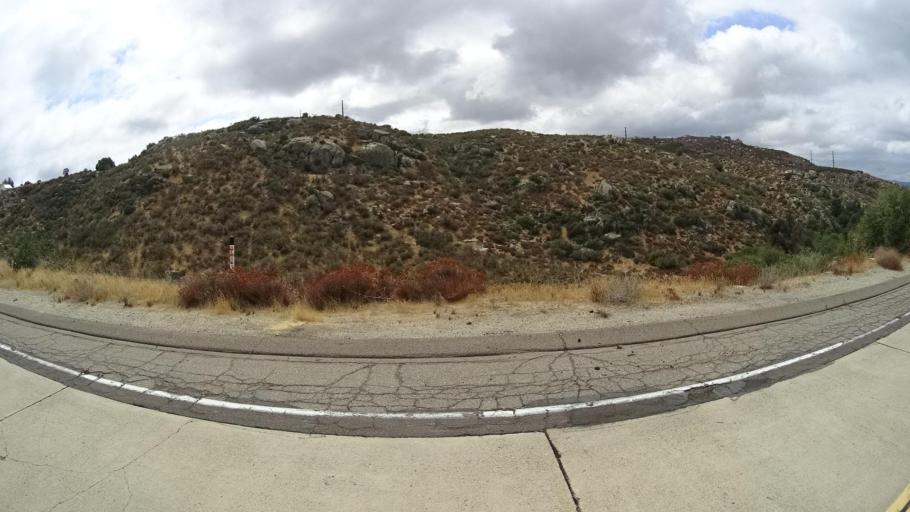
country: US
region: California
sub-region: San Diego County
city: Campo
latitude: 32.7052
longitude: -116.3692
